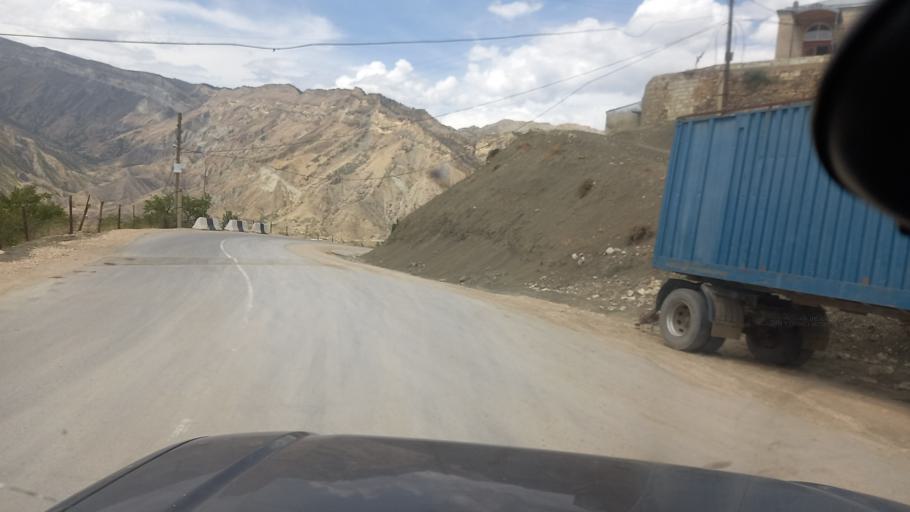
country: RU
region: Dagestan
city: Gunib
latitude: 42.3670
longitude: 46.9709
